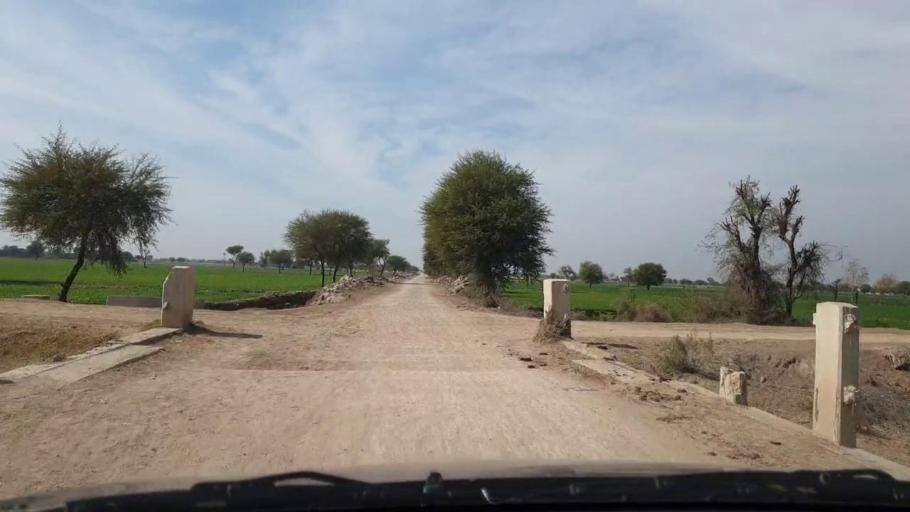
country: PK
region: Sindh
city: Jam Sahib
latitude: 26.2802
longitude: 68.6890
